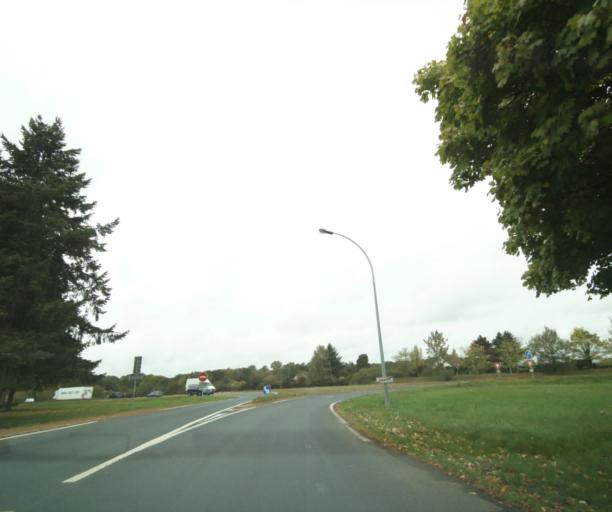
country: FR
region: Centre
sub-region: Departement d'Eure-et-Loir
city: Dreux
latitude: 48.7421
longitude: 1.3363
